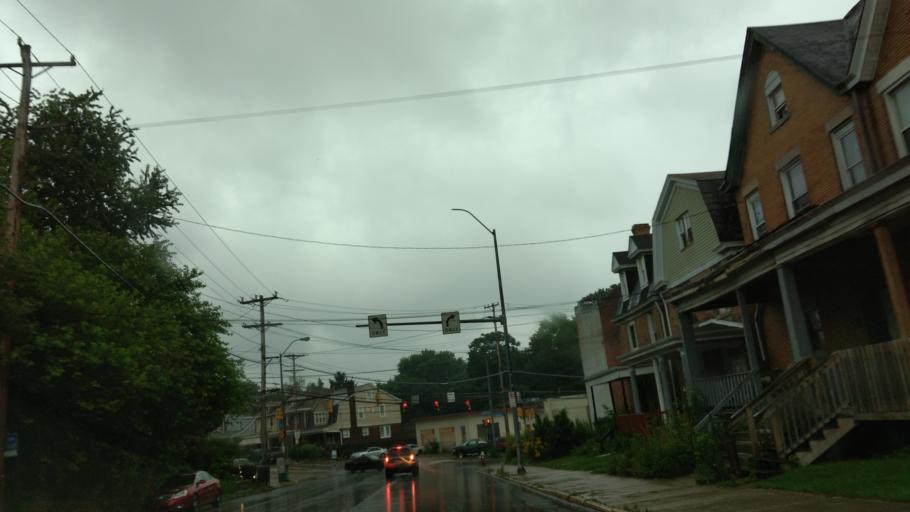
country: US
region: Pennsylvania
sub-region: Allegheny County
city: Bellevue
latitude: 40.4848
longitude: -80.0411
